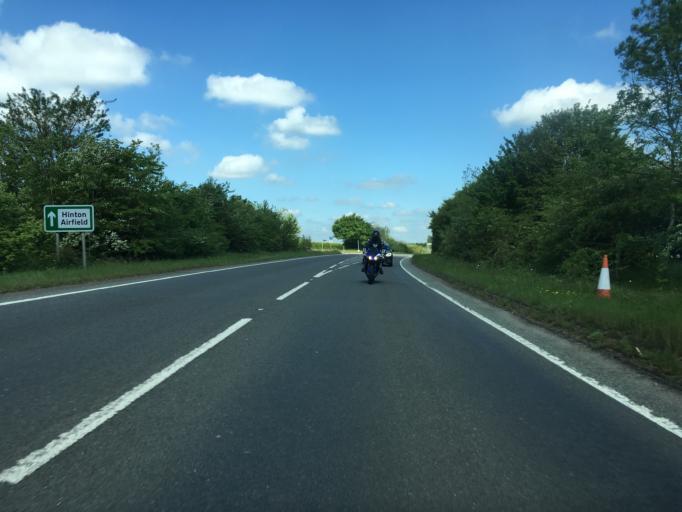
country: GB
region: England
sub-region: Northamptonshire
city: Brackley
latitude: 52.0239
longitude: -1.1564
